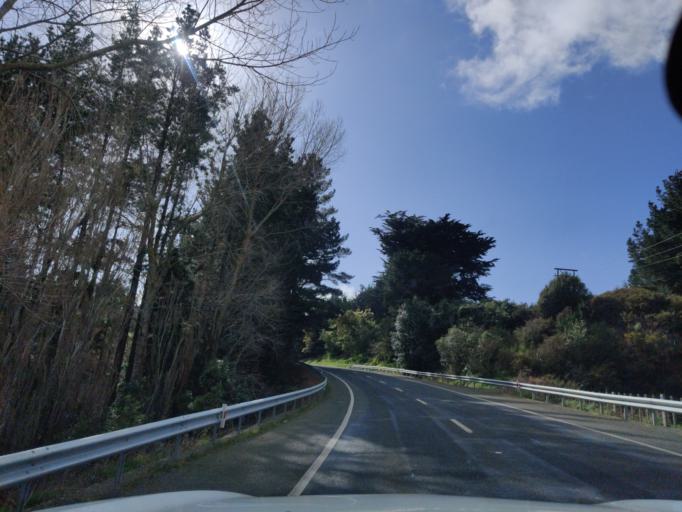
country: NZ
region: Manawatu-Wanganui
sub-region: Palmerston North City
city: Palmerston North
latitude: -40.4029
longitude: 175.6195
